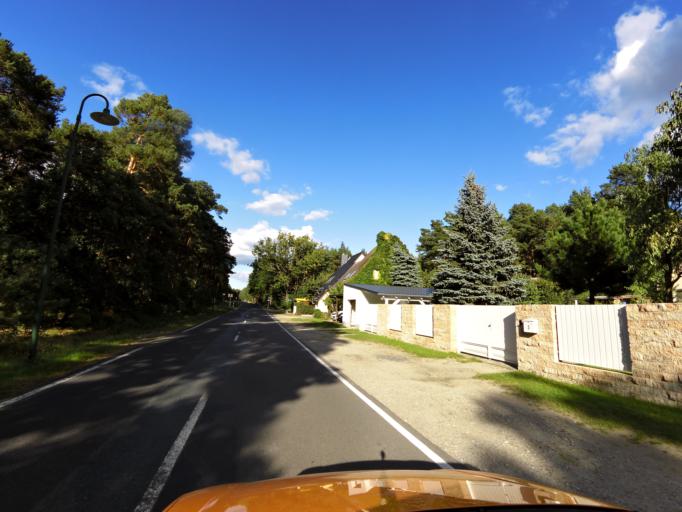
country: DE
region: Brandenburg
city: Luckenwalde
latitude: 52.1306
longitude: 13.1700
